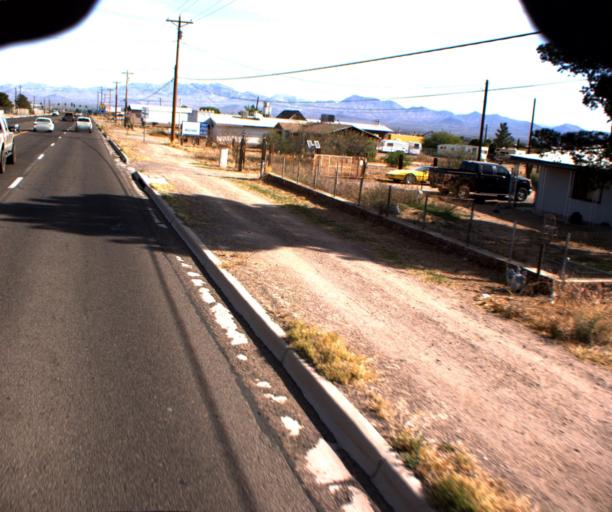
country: US
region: Arizona
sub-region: Graham County
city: Safford
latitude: 32.7989
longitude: -109.7077
